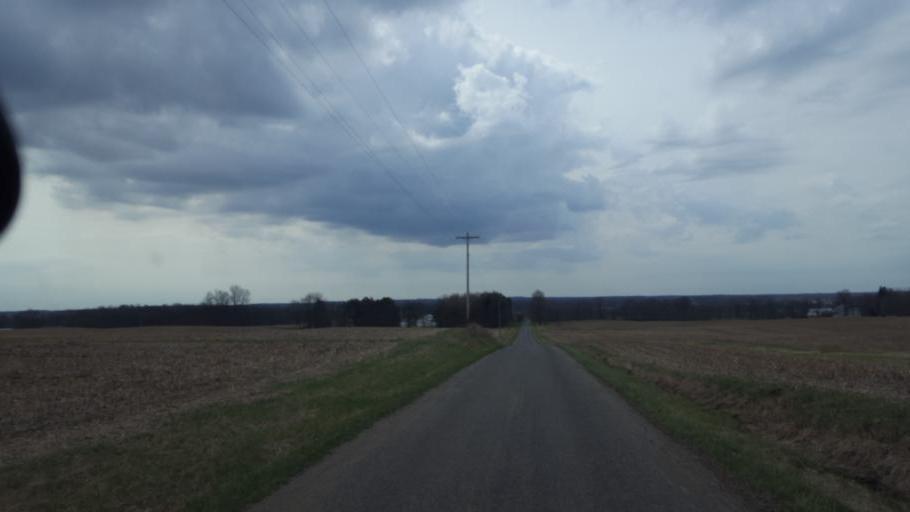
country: US
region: Ohio
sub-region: Knox County
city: Fredericktown
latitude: 40.4798
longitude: -82.6125
